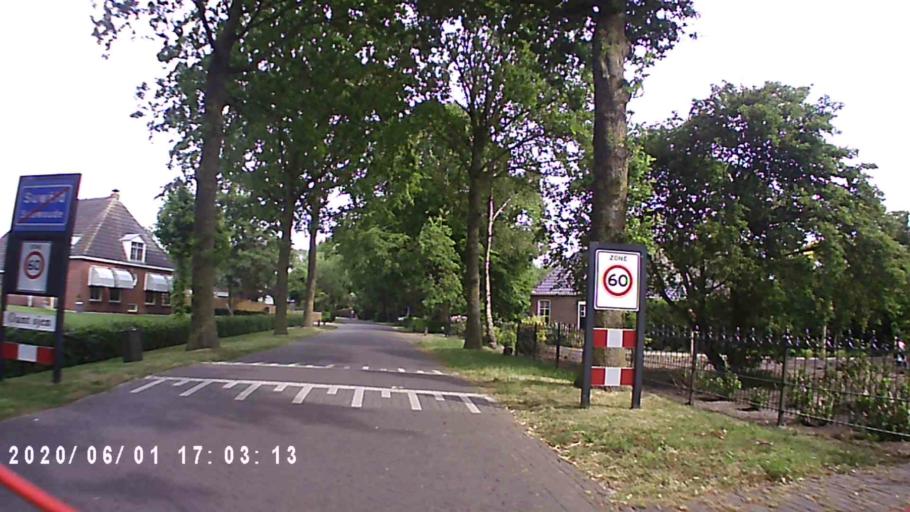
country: NL
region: Friesland
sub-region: Gemeente Tytsjerksteradiel
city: Hurdegaryp
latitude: 53.1771
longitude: 5.9296
